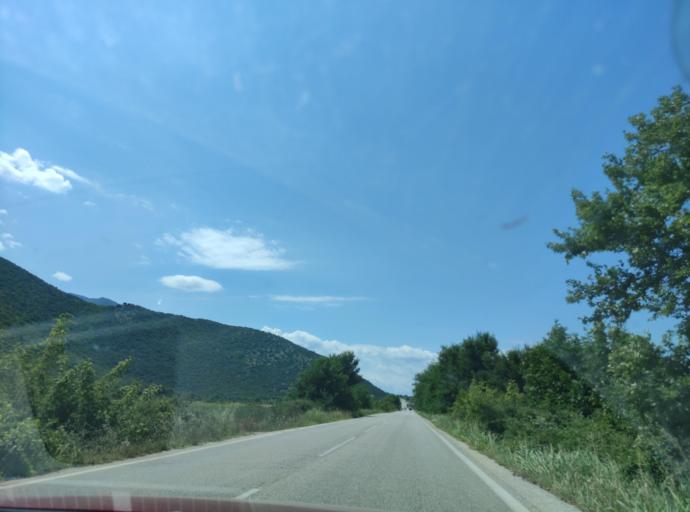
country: GR
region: East Macedonia and Thrace
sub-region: Nomos Kavalas
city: Palaiochori
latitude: 40.9683
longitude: 24.1754
